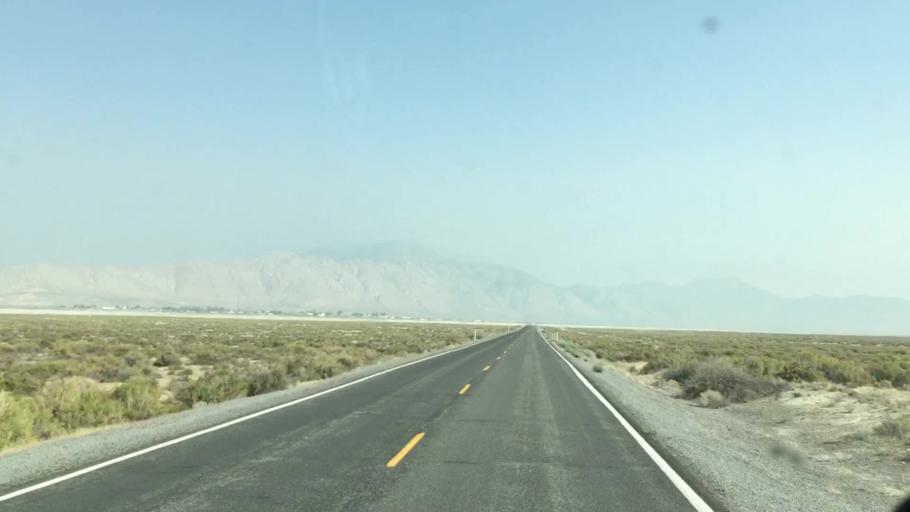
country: US
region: Nevada
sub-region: Pershing County
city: Lovelock
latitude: 40.6270
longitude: -119.3367
